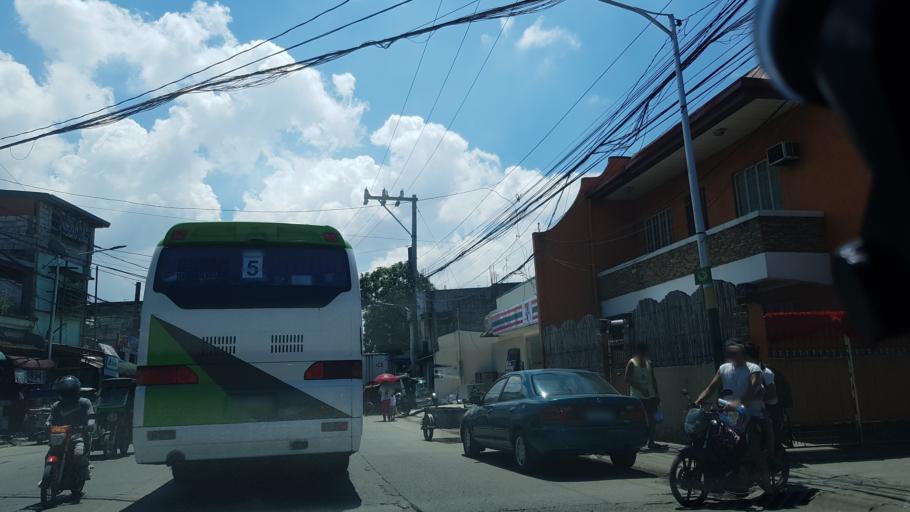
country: PH
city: Sambayanihan People's Village
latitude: 14.4720
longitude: 120.9988
